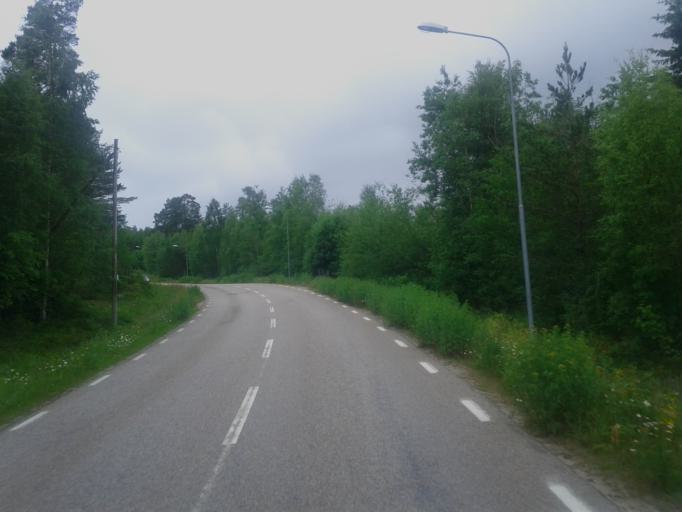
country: SE
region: Gaevleborg
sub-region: Nordanstigs Kommun
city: Bergsjoe
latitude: 61.9615
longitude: 17.3211
